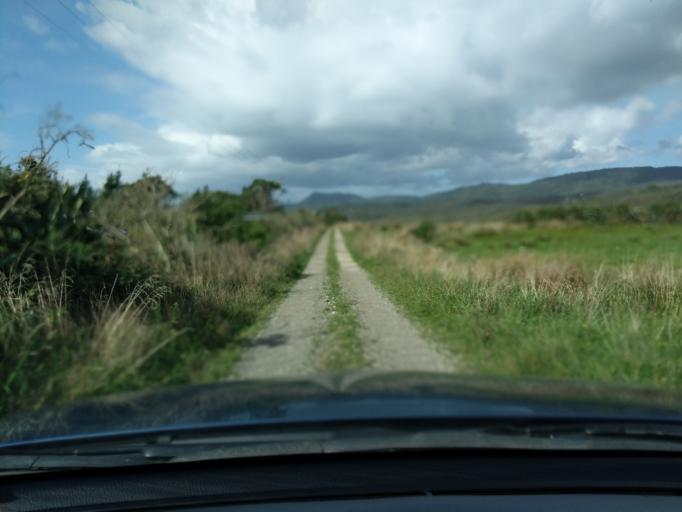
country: NZ
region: Tasman
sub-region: Tasman District
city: Takaka
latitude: -40.6516
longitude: 172.4740
